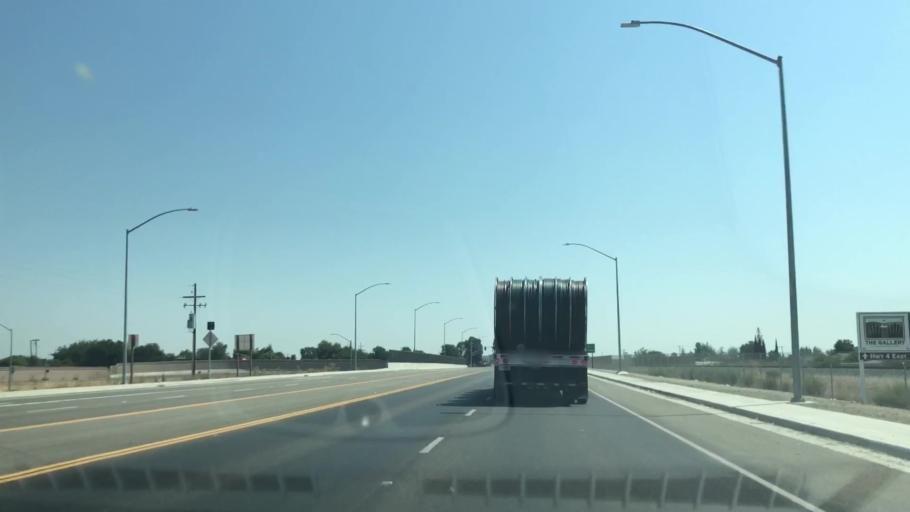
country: US
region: California
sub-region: San Joaquin County
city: Garden Acres
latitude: 37.9449
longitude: -121.2370
